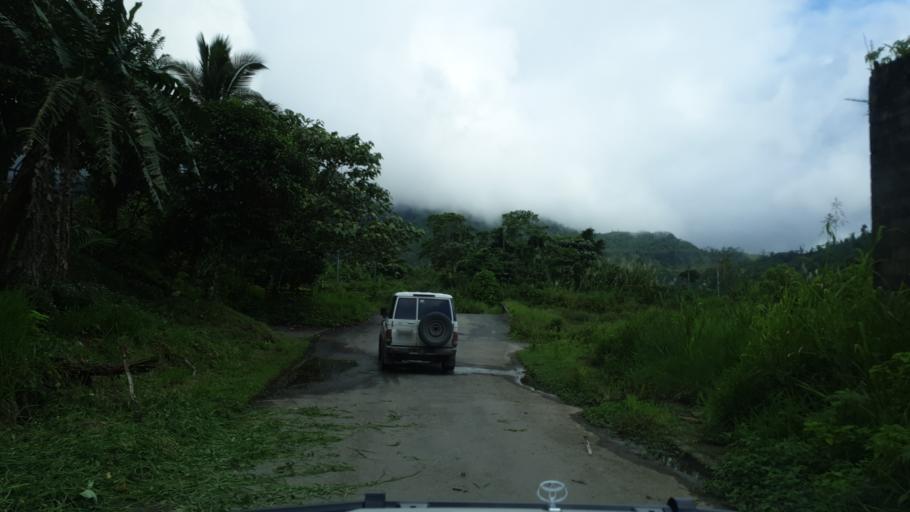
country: PG
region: Bougainville
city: Panguna
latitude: -6.3067
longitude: 155.4877
